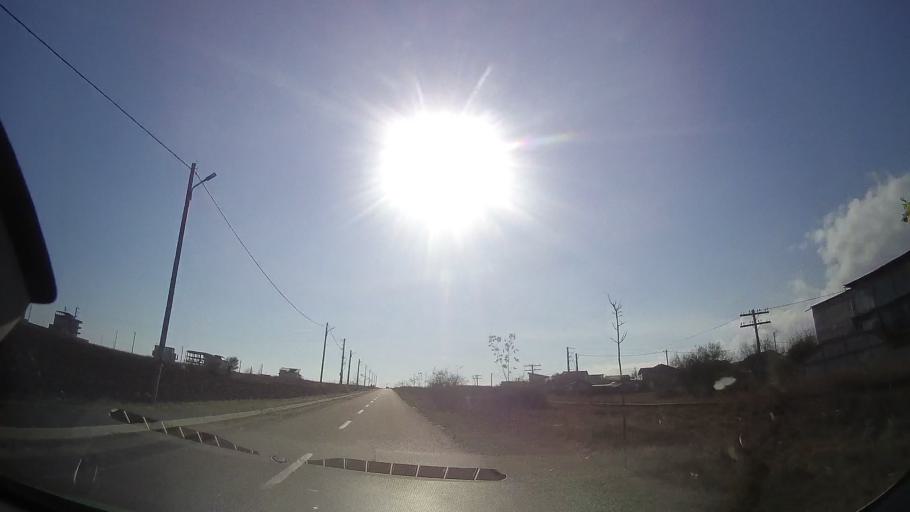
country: RO
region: Constanta
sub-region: Comuna Costinesti
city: Schitu
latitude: 43.9380
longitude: 28.6313
